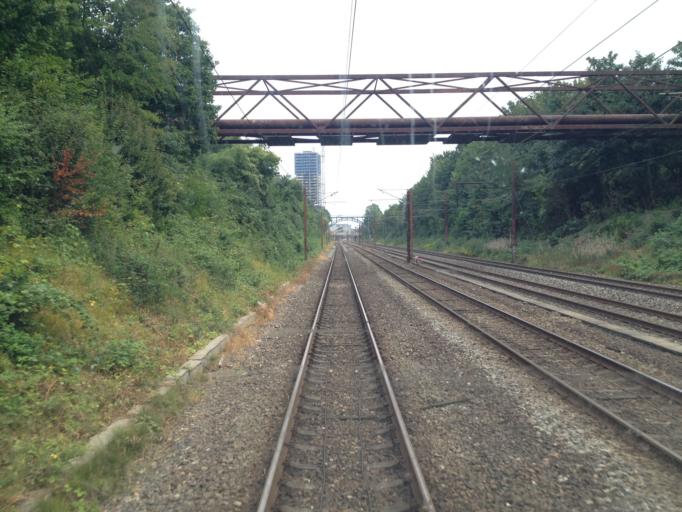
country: DK
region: Capital Region
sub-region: Frederiksberg Kommune
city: Frederiksberg
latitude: 55.6638
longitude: 12.5248
